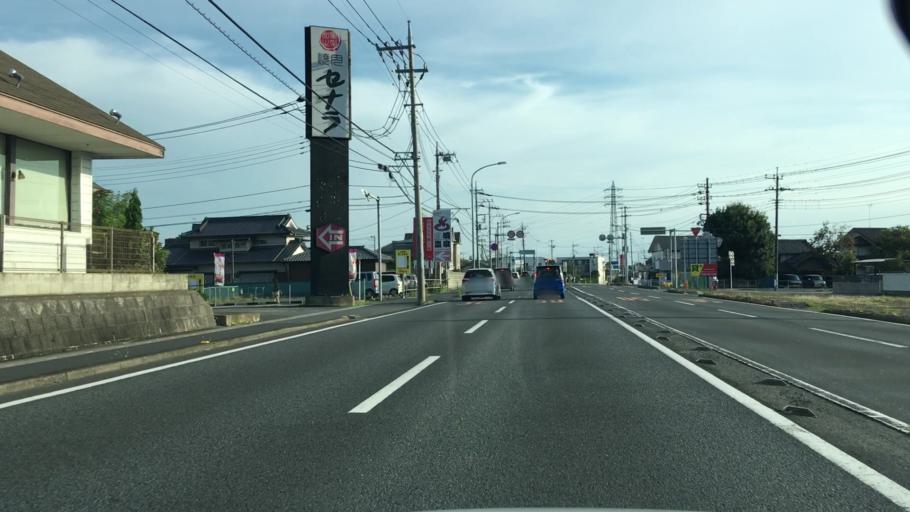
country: JP
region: Saitama
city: Kukichuo
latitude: 36.0914
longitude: 139.6760
